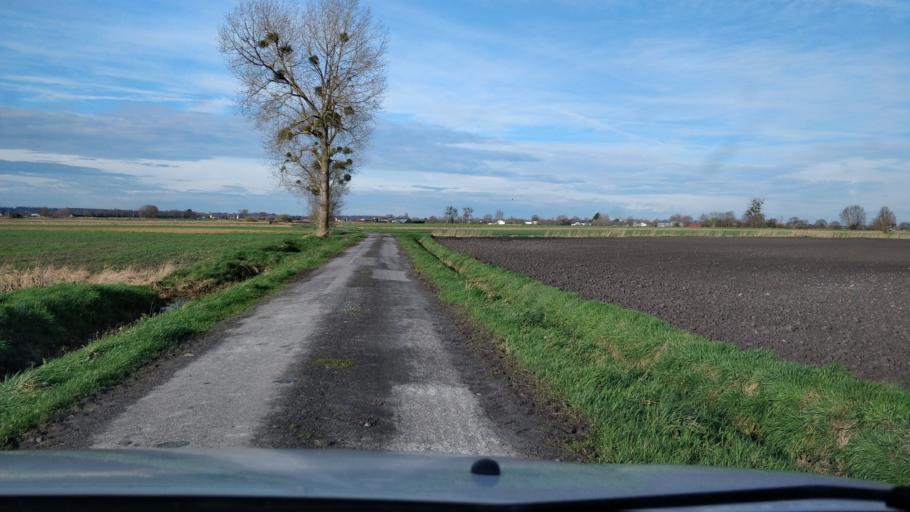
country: FR
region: Brittany
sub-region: Departement d'Ille-et-Vilaine
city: La Fresnais
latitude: 48.5761
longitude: -1.8245
